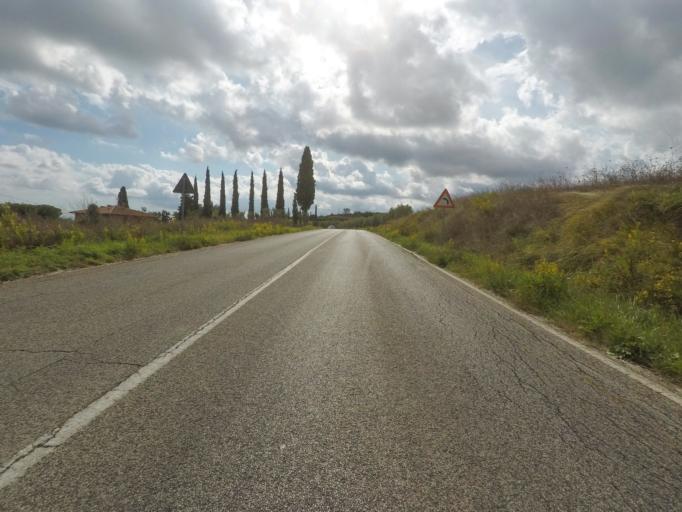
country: IT
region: Tuscany
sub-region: Provincia di Siena
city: Torrita di Siena
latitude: 43.1523
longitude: 11.7776
